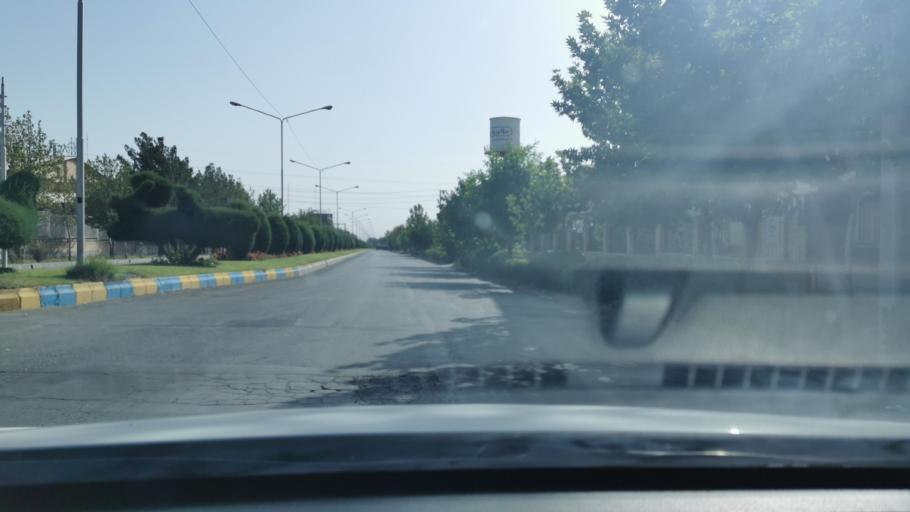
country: IR
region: Razavi Khorasan
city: Torqabeh
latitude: 36.4322
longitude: 59.4147
